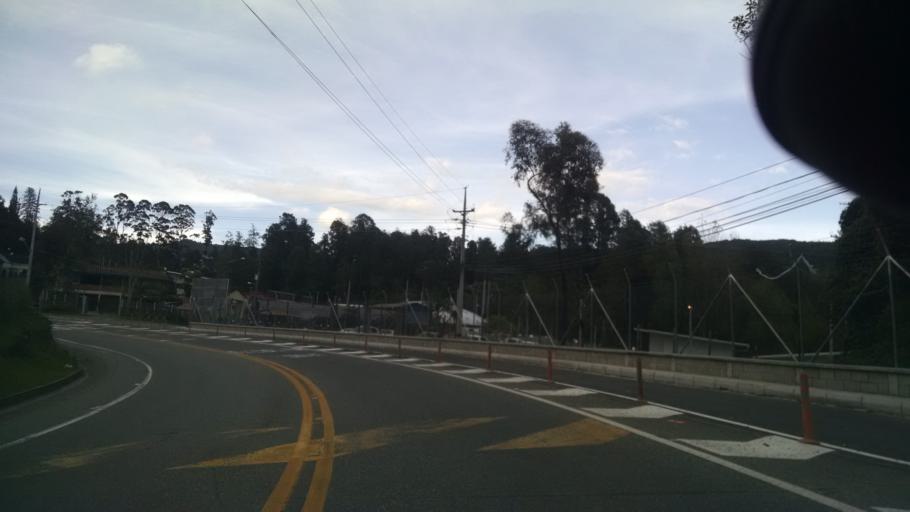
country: CO
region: Antioquia
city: El Retiro
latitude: 6.1075
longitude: -75.5009
